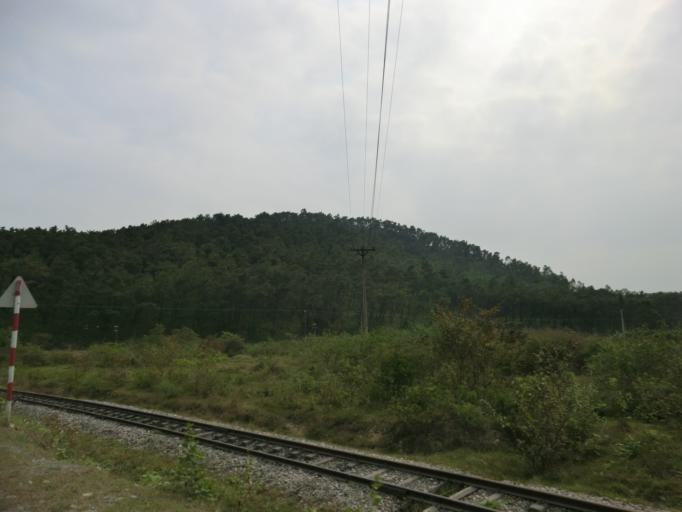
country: VN
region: Nghe An
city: Cau Giat
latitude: 19.1785
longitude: 105.5942
